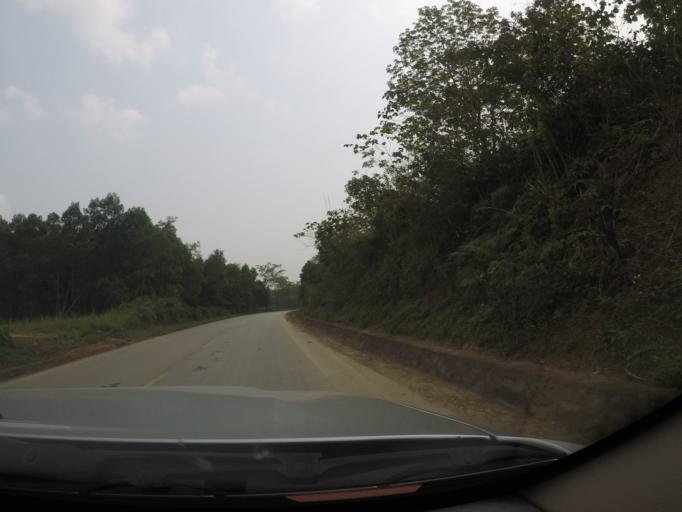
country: VN
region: Thanh Hoa
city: Thi Tran Yen Cat
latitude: 19.4896
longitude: 105.3936
